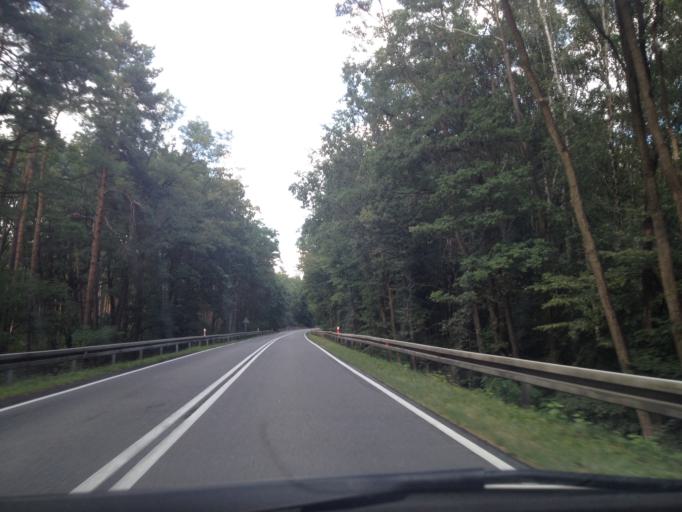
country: PL
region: Lubusz
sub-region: Powiat zarski
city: Sieniawa Zarska
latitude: 51.5850
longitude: 15.0778
